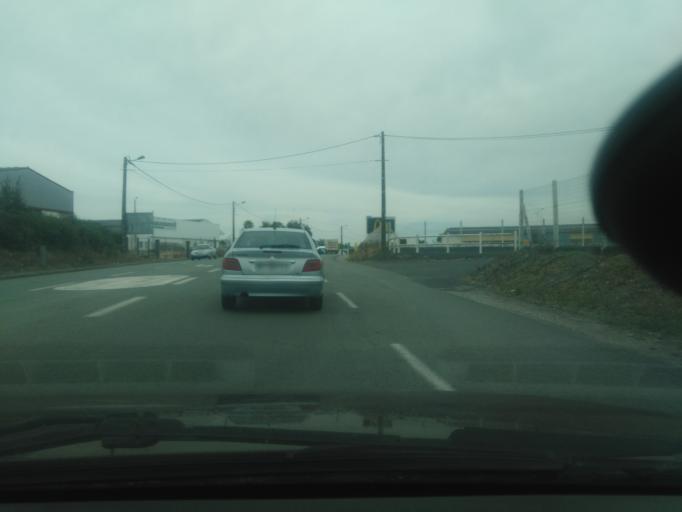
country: FR
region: Poitou-Charentes
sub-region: Departement des Deux-Sevres
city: Chatillon-sur-Thouet
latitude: 46.6432
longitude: -0.2288
